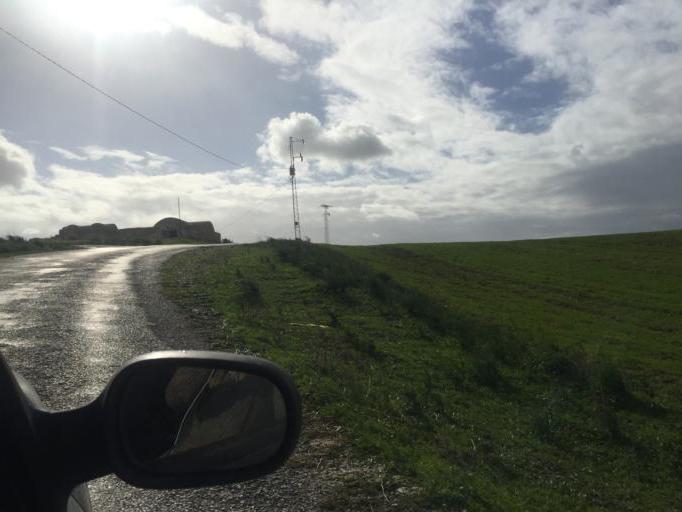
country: TN
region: Nabul
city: El Mida
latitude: 36.8081
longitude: 10.8457
